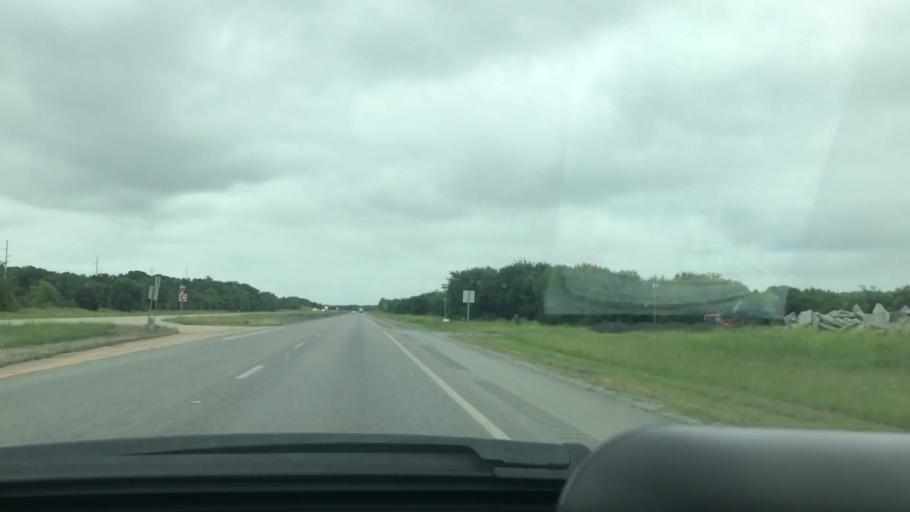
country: US
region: Oklahoma
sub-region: Coal County
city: Coalgate
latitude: 34.6364
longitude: -95.9526
